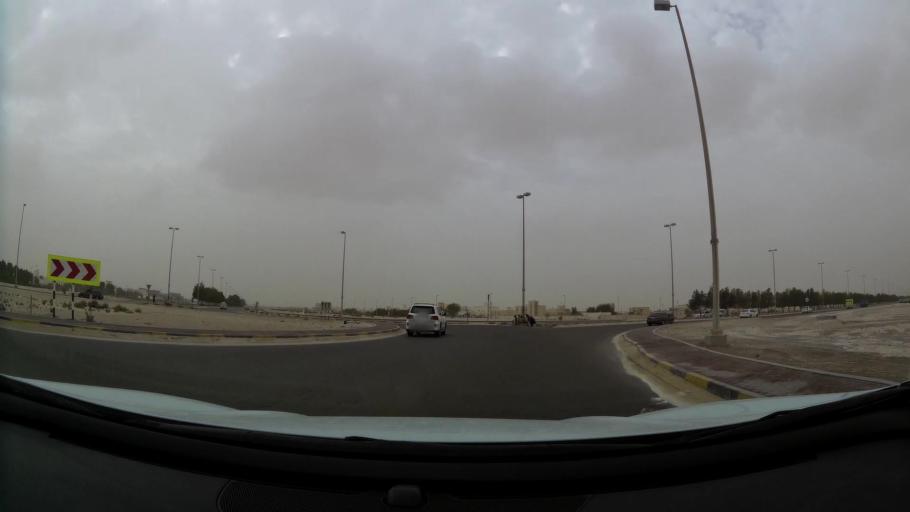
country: AE
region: Abu Dhabi
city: Abu Dhabi
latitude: 24.4013
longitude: 54.7167
